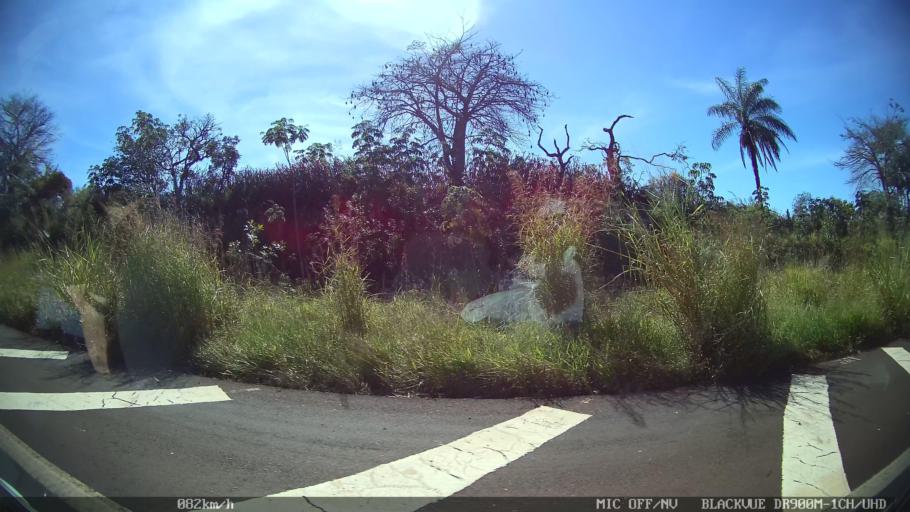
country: BR
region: Sao Paulo
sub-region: Franca
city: Franca
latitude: -20.5605
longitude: -47.5272
